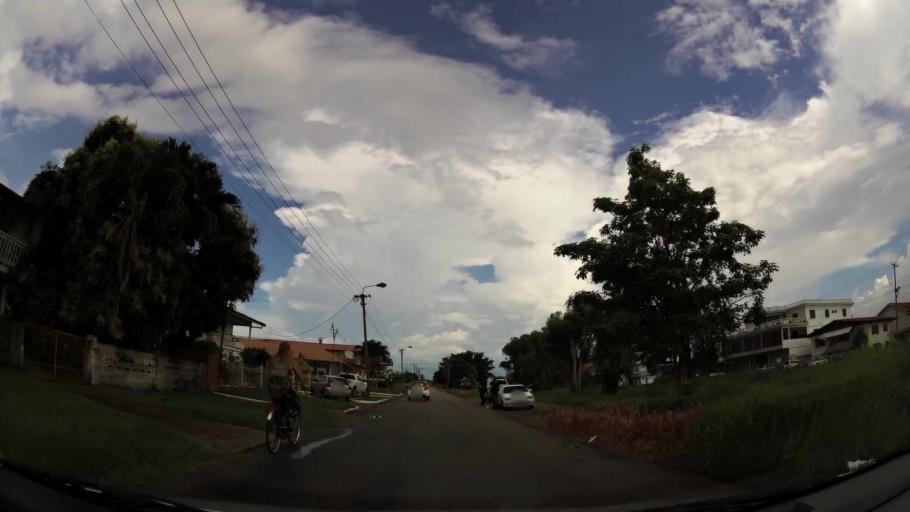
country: SR
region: Paramaribo
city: Paramaribo
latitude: 5.8396
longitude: -55.1376
